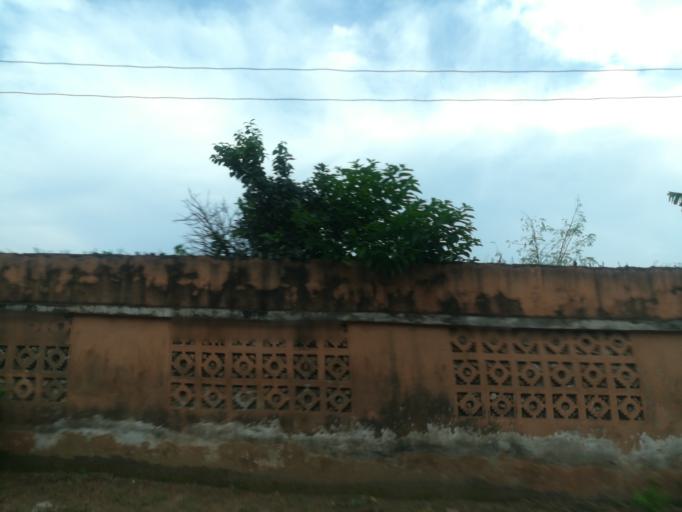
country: NG
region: Oyo
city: Ibadan
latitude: 7.4141
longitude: 3.9043
